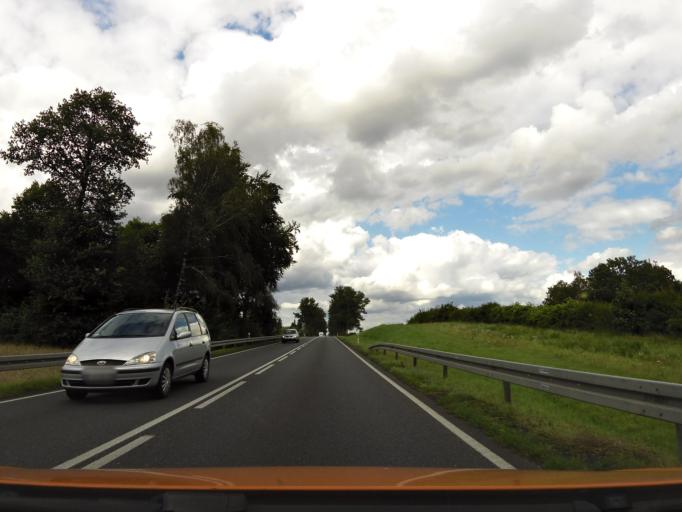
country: PL
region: West Pomeranian Voivodeship
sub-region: Powiat gryficki
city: Brojce
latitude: 53.8621
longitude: 15.3509
